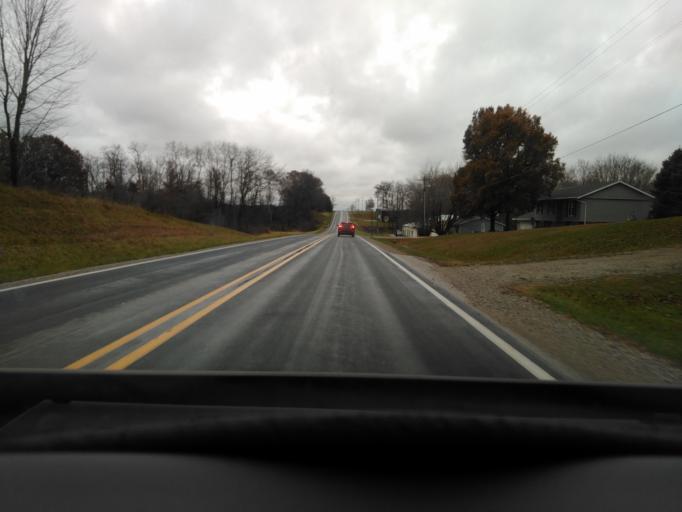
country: US
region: Illinois
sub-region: Effingham County
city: Altamont
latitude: 39.0349
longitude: -88.7483
